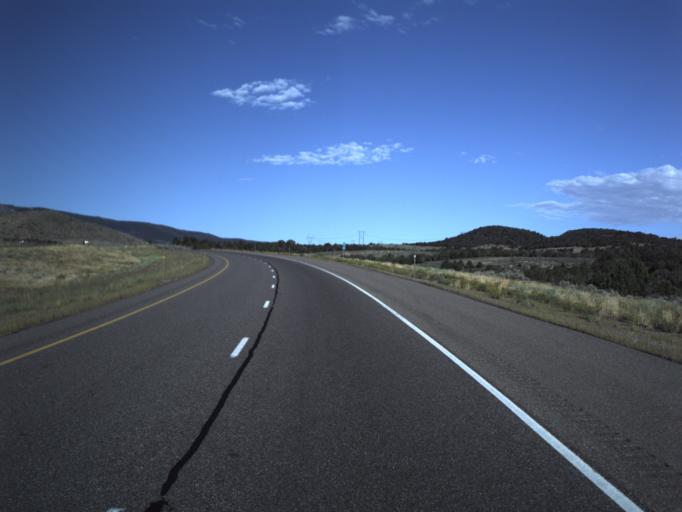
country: US
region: Utah
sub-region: Sevier County
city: Monroe
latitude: 38.5512
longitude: -112.3901
